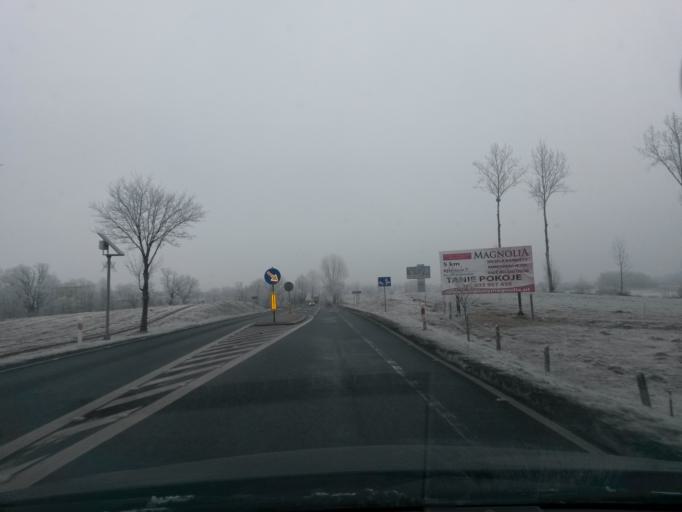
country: PL
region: Greater Poland Voivodeship
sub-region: Powiat gnieznienski
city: Trzemeszno
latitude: 52.5595
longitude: 17.7777
